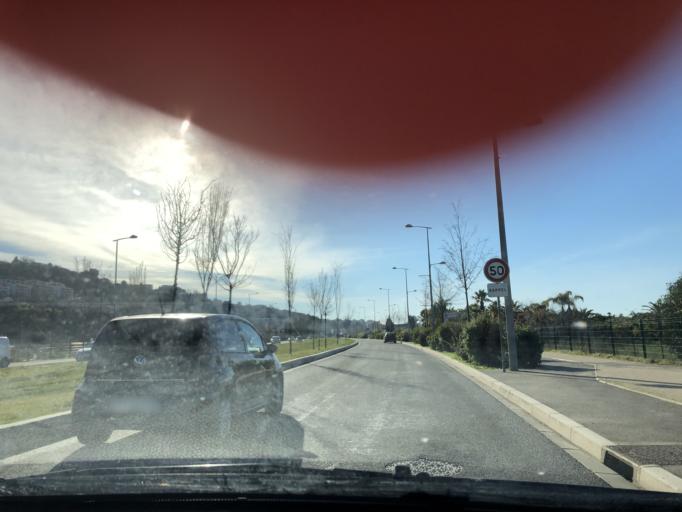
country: FR
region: Provence-Alpes-Cote d'Azur
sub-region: Departement des Alpes-Maritimes
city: Saint-Laurent-du-Var
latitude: 43.6967
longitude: 7.1967
